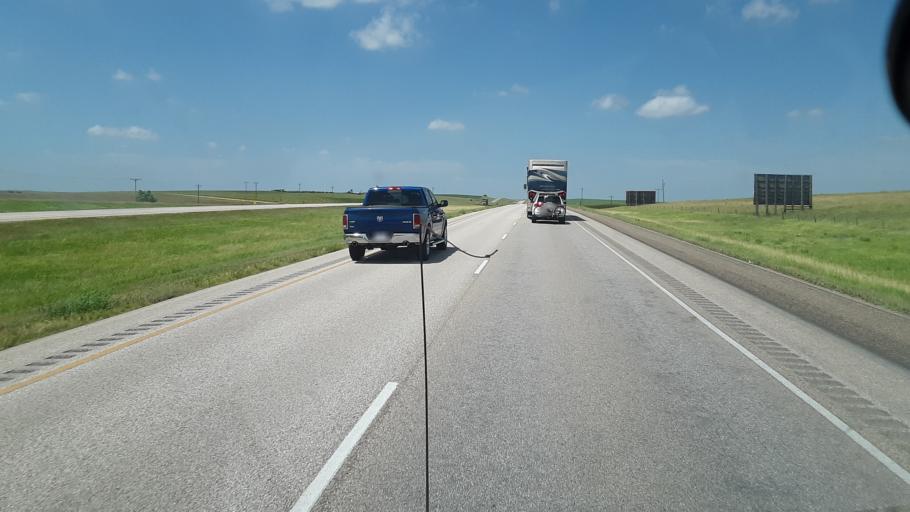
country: US
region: South Dakota
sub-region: Jackson County
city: Kadoka
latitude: 43.8365
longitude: -101.5570
